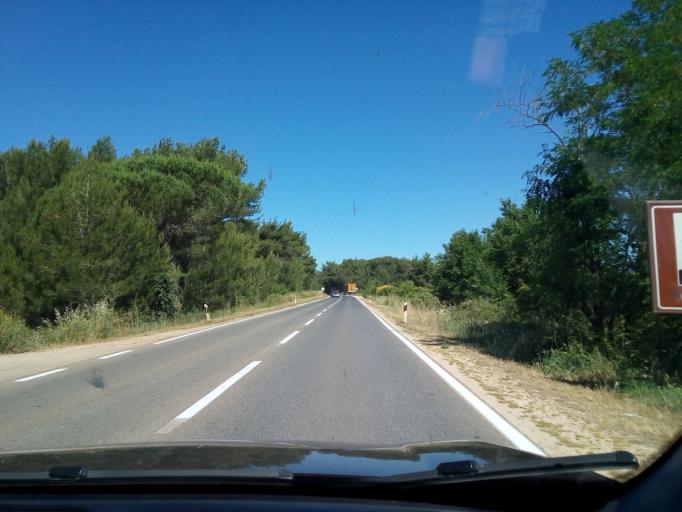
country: HR
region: Zadarska
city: Zadar
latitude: 44.1509
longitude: 15.2200
